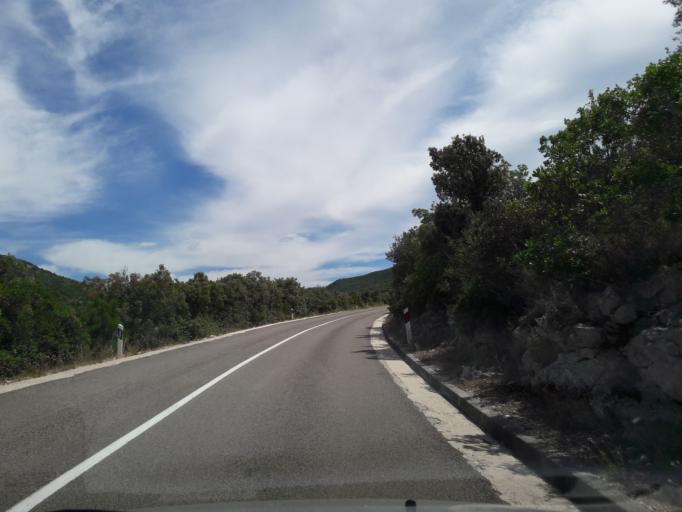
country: HR
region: Dubrovacko-Neretvanska
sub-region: Grad Dubrovnik
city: Opuzen
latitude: 42.9128
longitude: 17.4761
